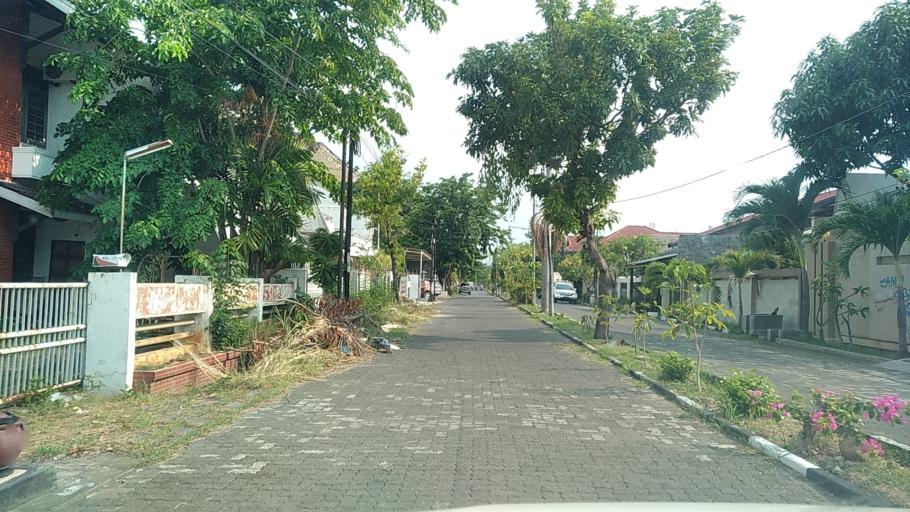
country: ID
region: Central Java
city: Semarang
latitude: -6.9688
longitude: 110.4078
